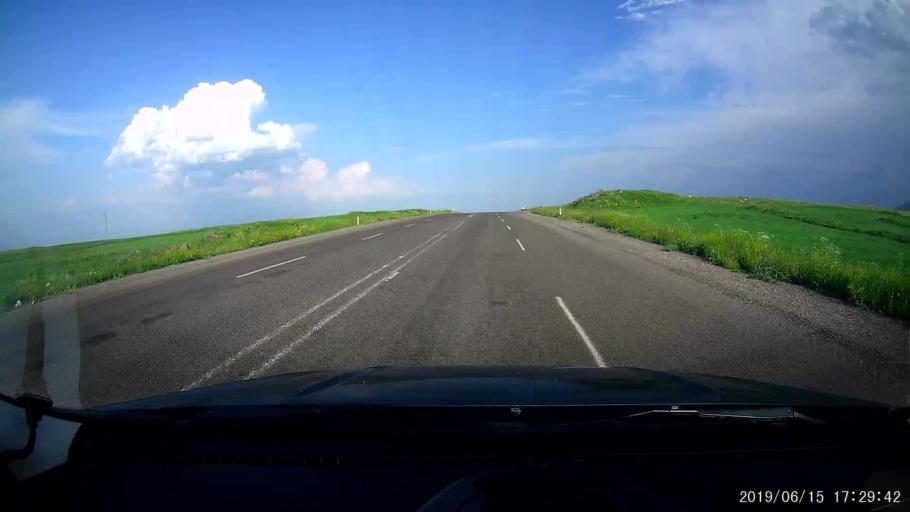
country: TR
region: Kars
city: Basgedikler
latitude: 40.5878
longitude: 43.4566
